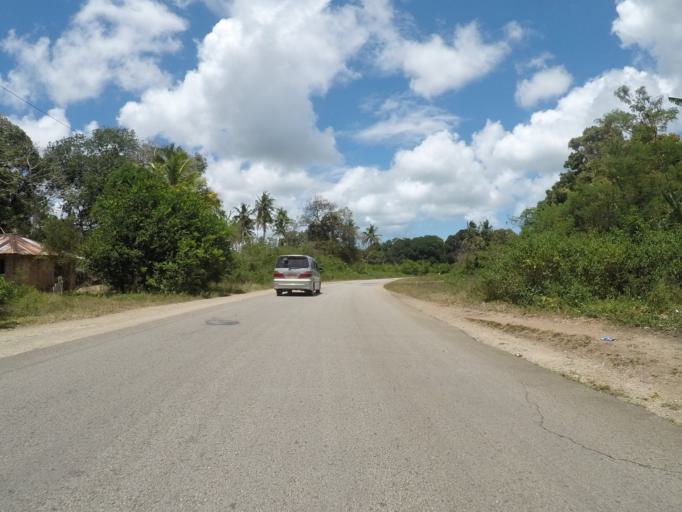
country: TZ
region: Zanzibar Central/South
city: Nganane
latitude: -6.2911
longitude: 39.4393
